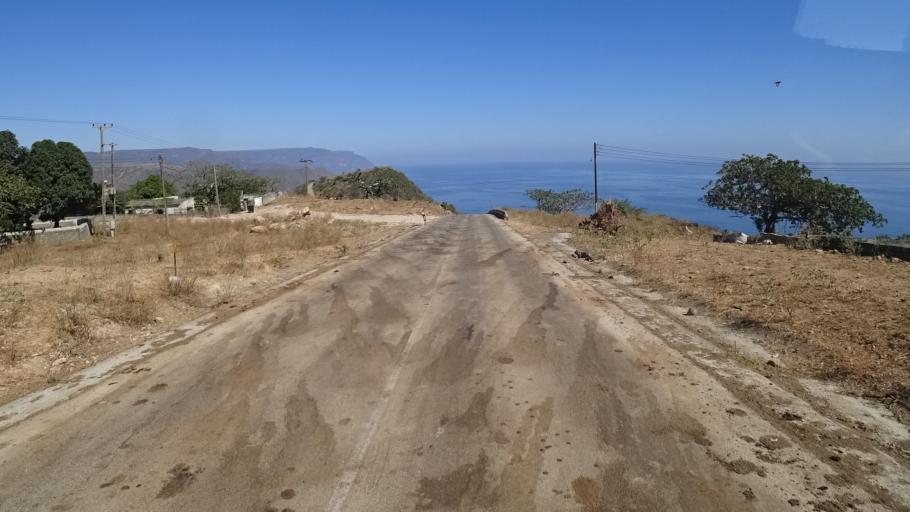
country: YE
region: Al Mahrah
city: Hawf
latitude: 16.7435
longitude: 53.3787
